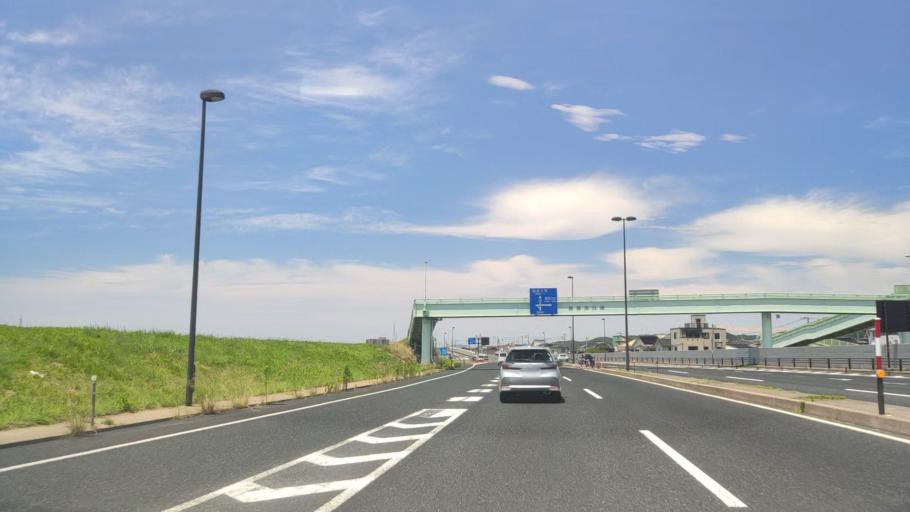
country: JP
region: Tottori
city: Tottori
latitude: 35.5010
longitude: 134.2181
